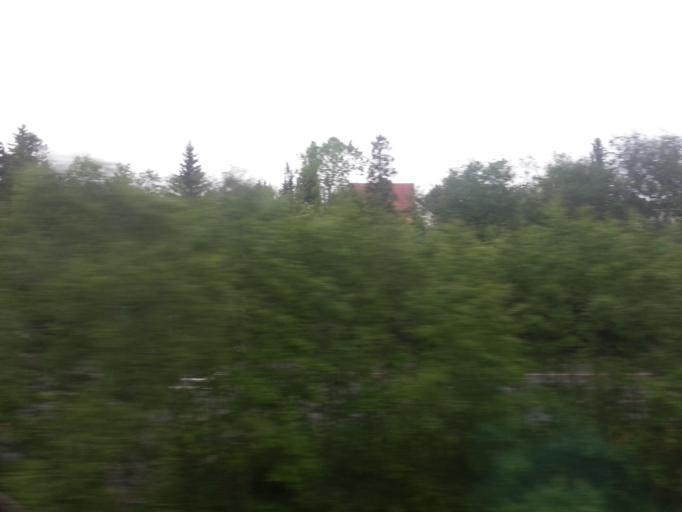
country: NO
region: Sor-Trondelag
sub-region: Trondheim
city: Trondheim
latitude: 63.3567
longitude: 10.3586
